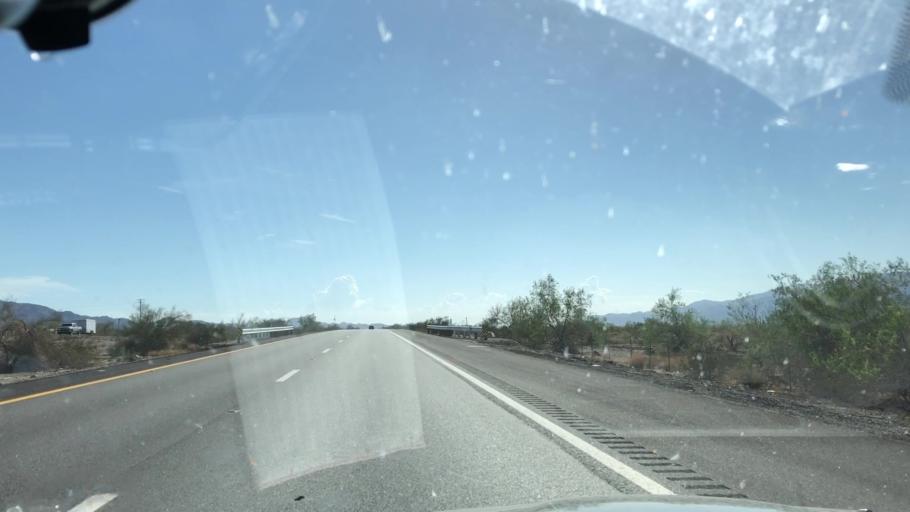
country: US
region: California
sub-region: Imperial County
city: Niland
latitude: 33.6889
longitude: -115.5144
